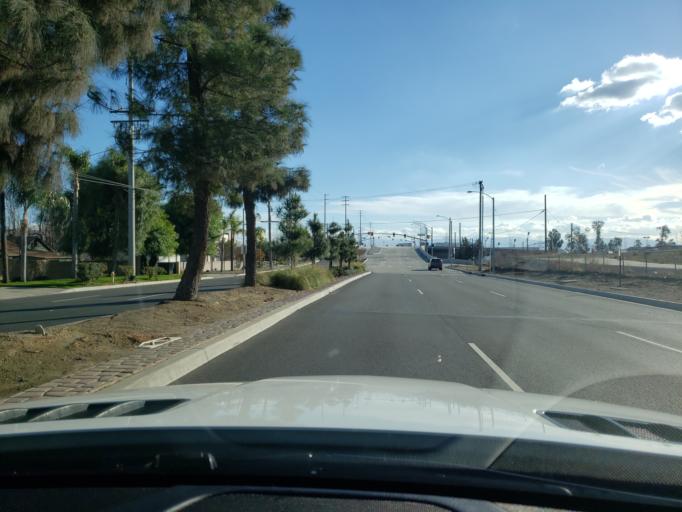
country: US
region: California
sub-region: Riverside County
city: Mira Loma
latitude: 34.0359
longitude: -117.5584
